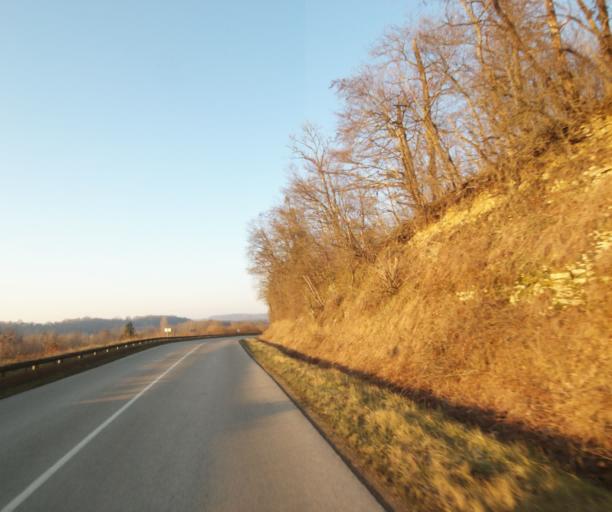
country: FR
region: Champagne-Ardenne
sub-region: Departement de la Haute-Marne
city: Bienville
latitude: 48.5898
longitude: 5.0426
